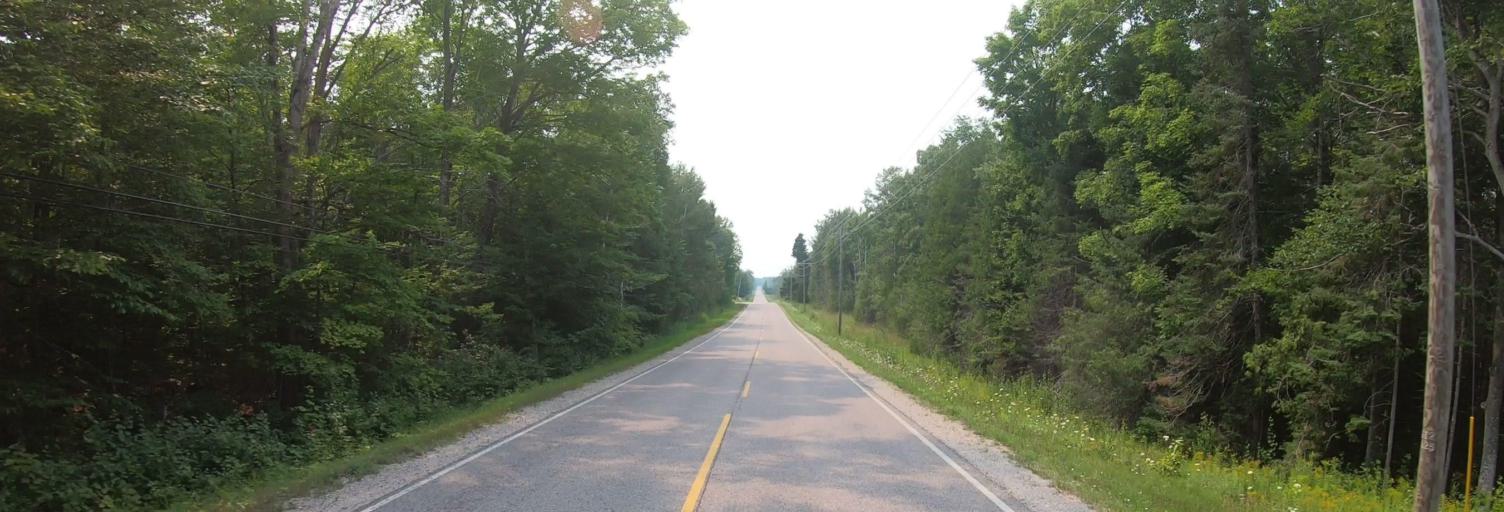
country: CA
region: Ontario
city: Thessalon
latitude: 46.0002
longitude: -83.9562
